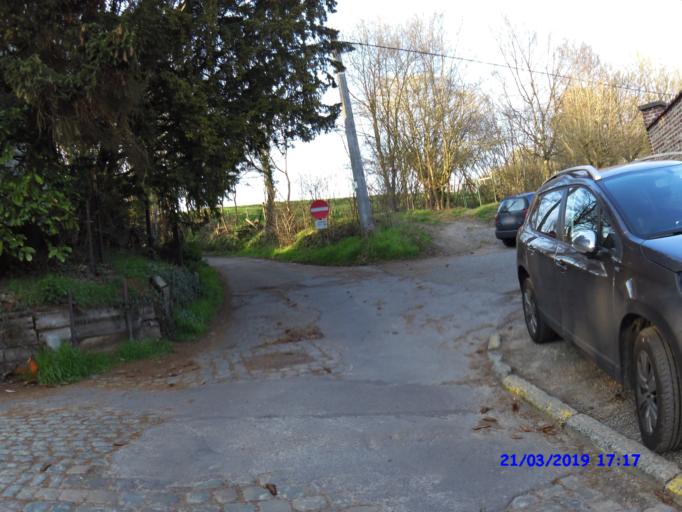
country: BE
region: Flanders
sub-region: Provincie Vlaams-Brabant
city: Sint-Genesius-Rode
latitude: 50.7455
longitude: 4.3425
